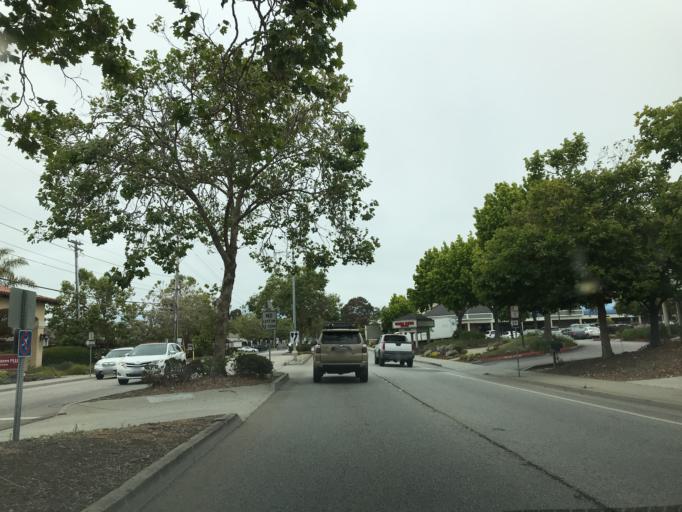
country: US
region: California
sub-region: Santa Cruz County
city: Opal Cliffs
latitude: 36.9707
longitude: -121.9649
